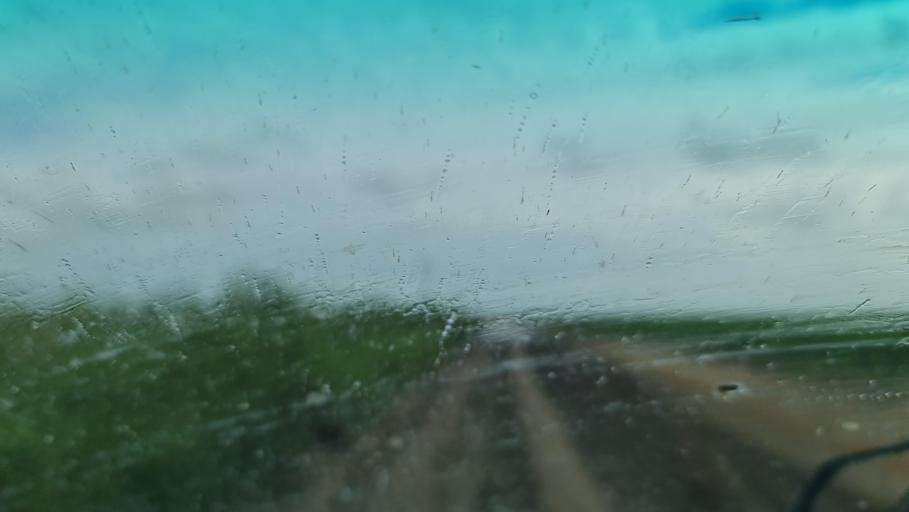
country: MZ
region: Maputo
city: Manhica
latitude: -25.4434
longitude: 32.8400
